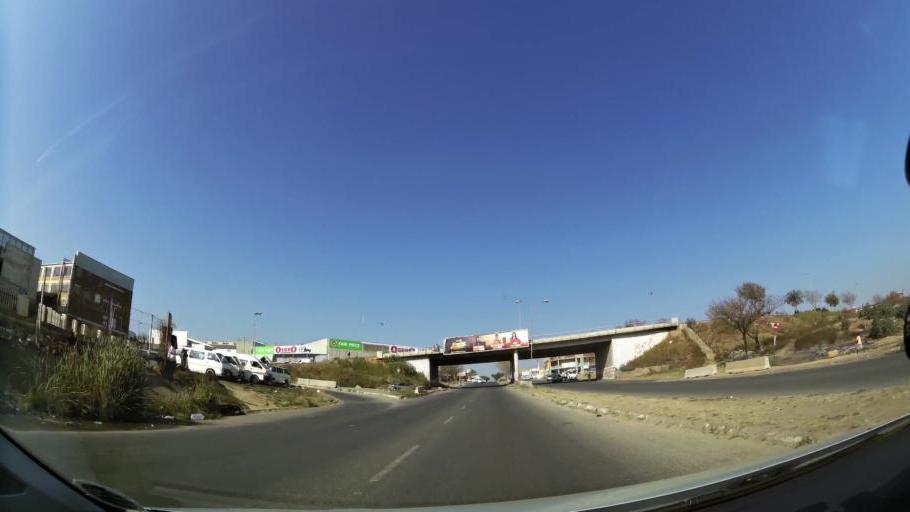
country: ZA
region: Gauteng
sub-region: City of Johannesburg Metropolitan Municipality
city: Modderfontein
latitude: -26.1093
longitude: 28.0850
